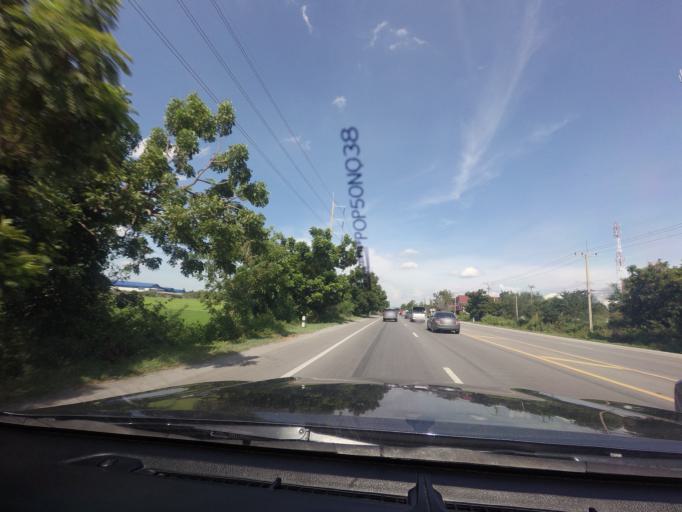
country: TH
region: Suphan Buri
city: Song Phi Nong
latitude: 14.1579
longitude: 100.1418
